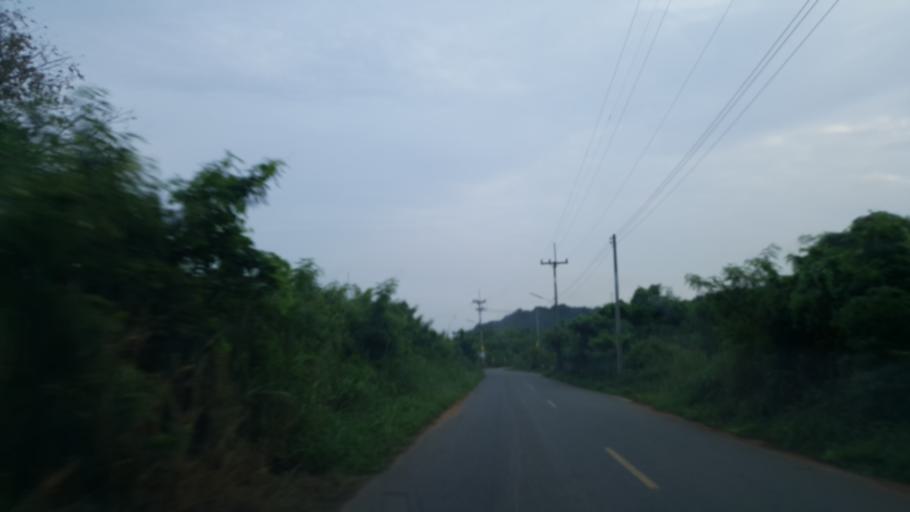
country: TH
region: Chon Buri
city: Sattahip
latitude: 12.7044
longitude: 100.9066
